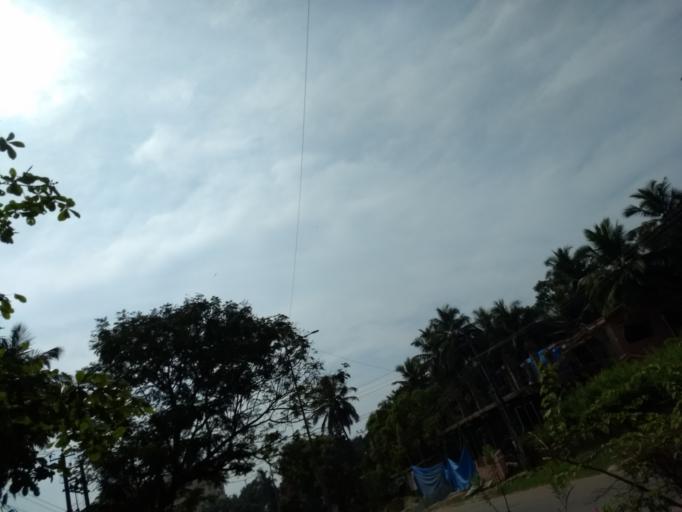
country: IN
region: Karnataka
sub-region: Dakshina Kannada
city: Mangalore
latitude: 12.8992
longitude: 74.8435
